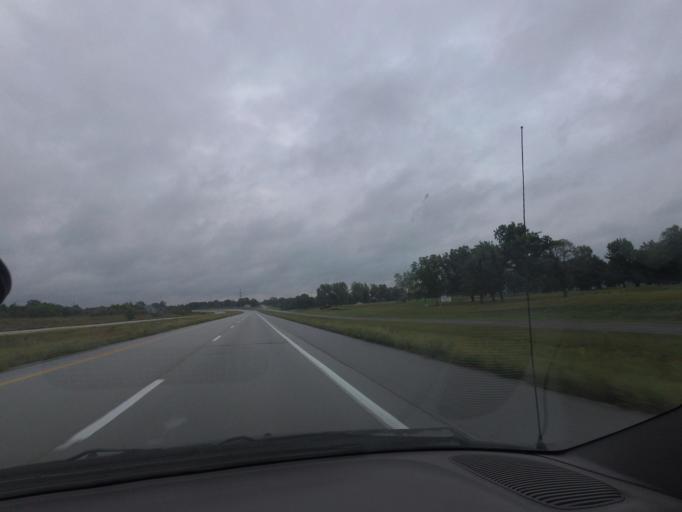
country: US
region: Missouri
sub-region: Marion County
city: Monroe City
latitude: 39.6579
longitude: -91.7574
